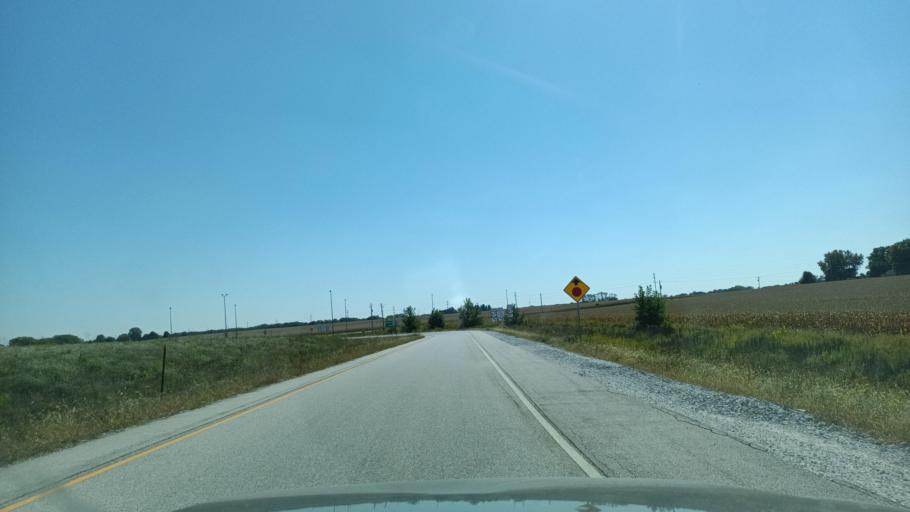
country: US
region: Illinois
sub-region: McDonough County
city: Macomb
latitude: 40.5026
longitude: -90.6771
